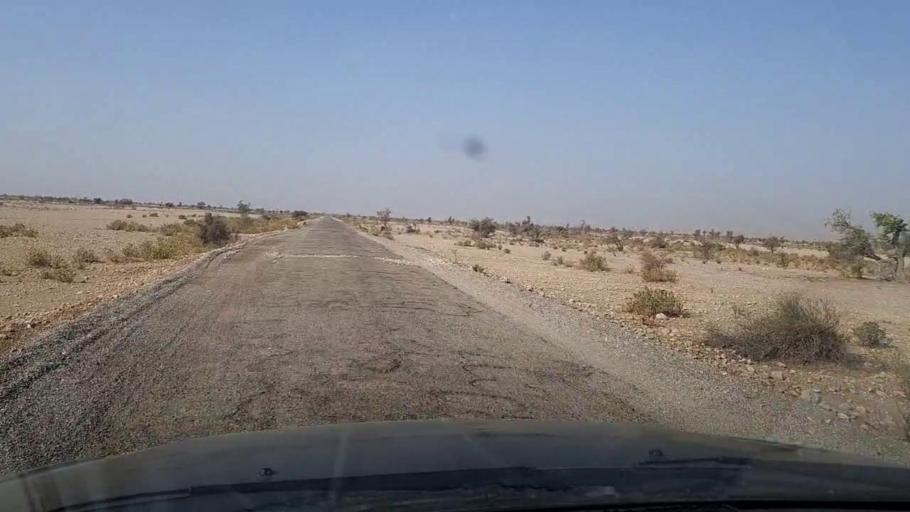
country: PK
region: Sindh
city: Sann
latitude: 25.9182
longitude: 68.0133
